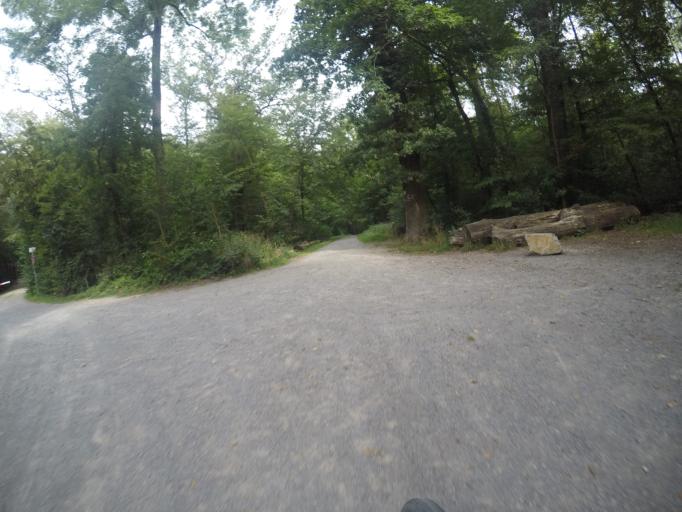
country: DE
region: Baden-Wuerttemberg
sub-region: Regierungsbezirk Stuttgart
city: Stuttgart
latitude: 48.7458
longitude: 9.1449
